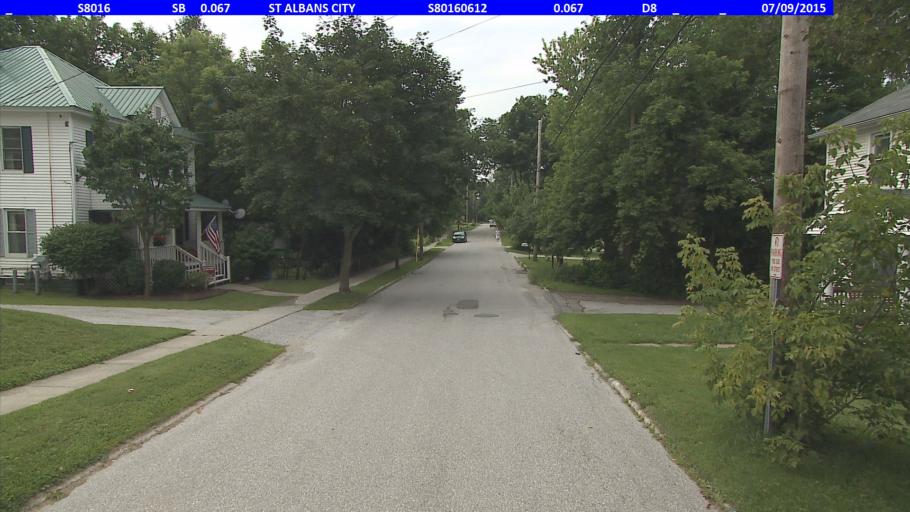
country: US
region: Vermont
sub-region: Franklin County
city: Saint Albans
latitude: 44.8068
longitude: -73.0814
